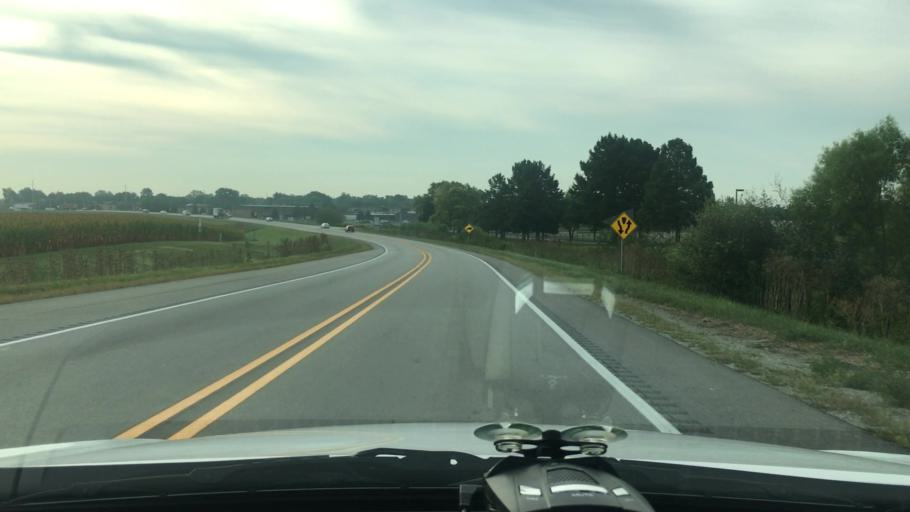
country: US
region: Illinois
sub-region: Champaign County
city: Champaign
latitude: 40.1408
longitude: -88.2843
